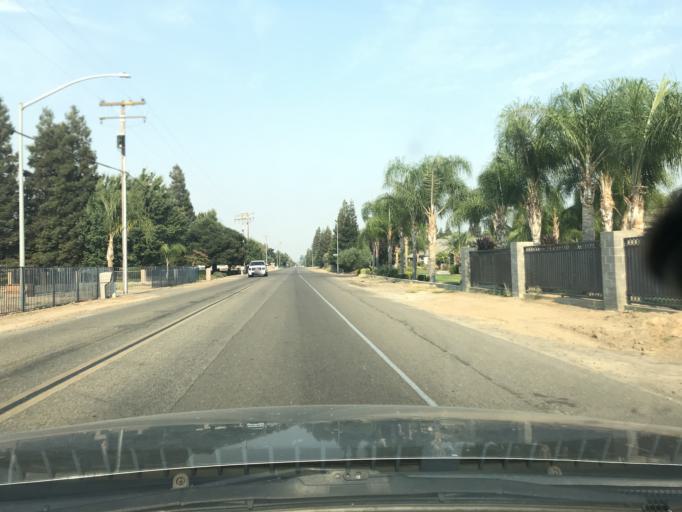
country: US
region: California
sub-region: Merced County
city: Atwater
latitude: 37.3239
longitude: -120.5999
